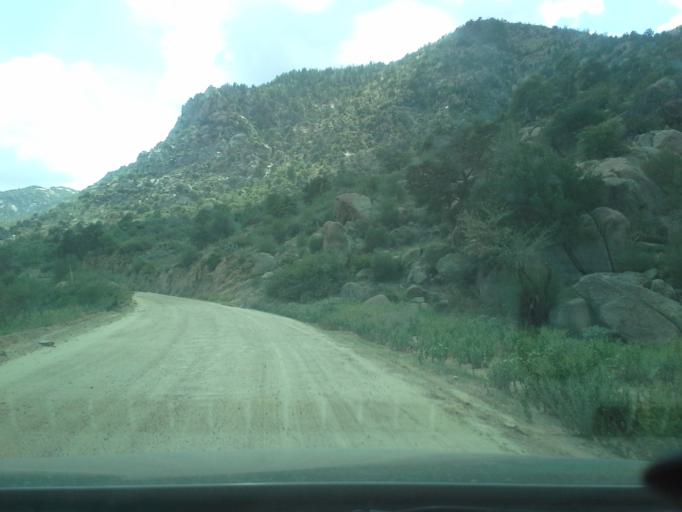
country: US
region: Arizona
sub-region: Yavapai County
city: Mayer
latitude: 34.2335
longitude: -112.3052
